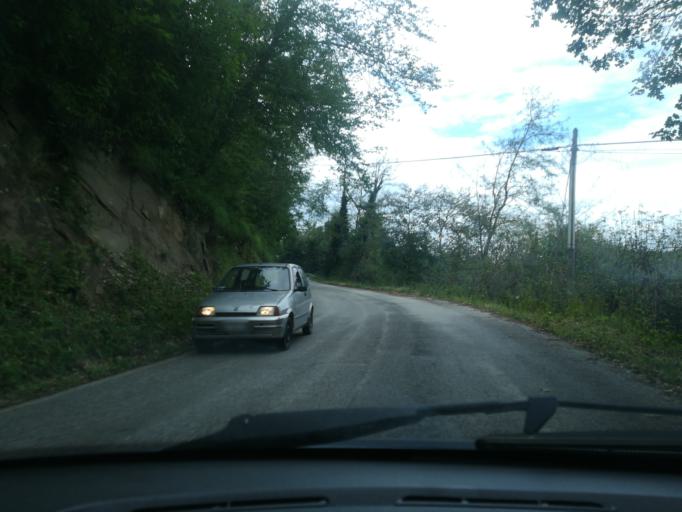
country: IT
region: The Marches
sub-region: Province of Fermo
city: Montefortino
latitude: 42.9395
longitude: 13.3538
